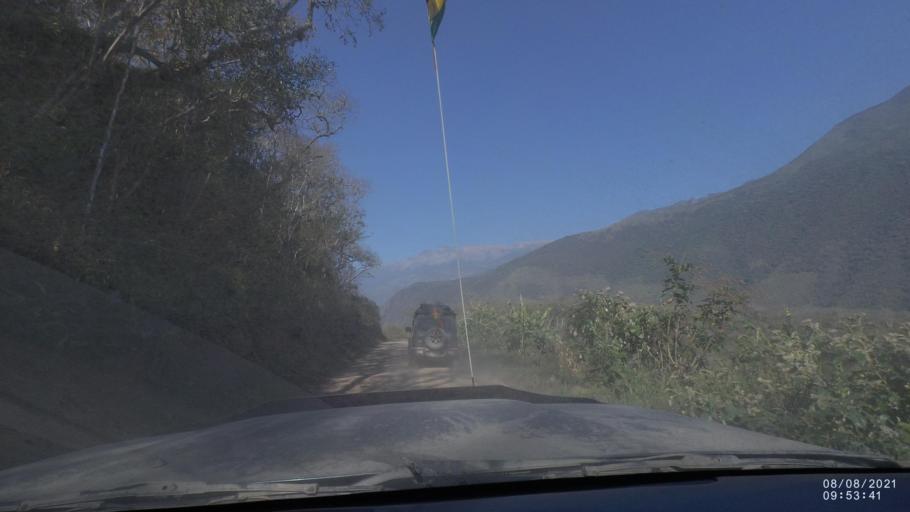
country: BO
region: La Paz
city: Quime
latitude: -16.6298
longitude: -66.7337
